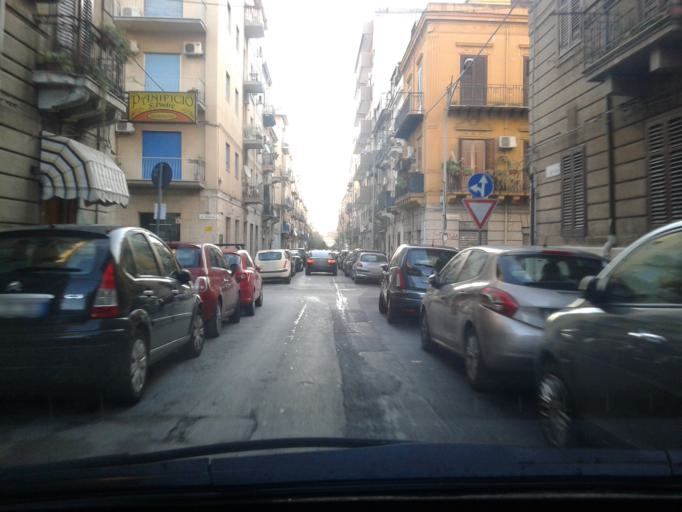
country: IT
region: Sicily
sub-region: Palermo
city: Palermo
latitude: 38.1203
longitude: 13.3451
